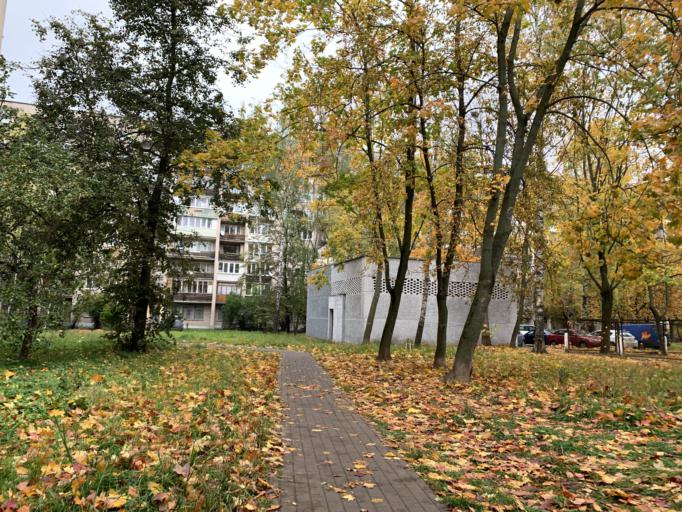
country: BY
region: Minsk
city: Minsk
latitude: 53.9374
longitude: 27.6009
